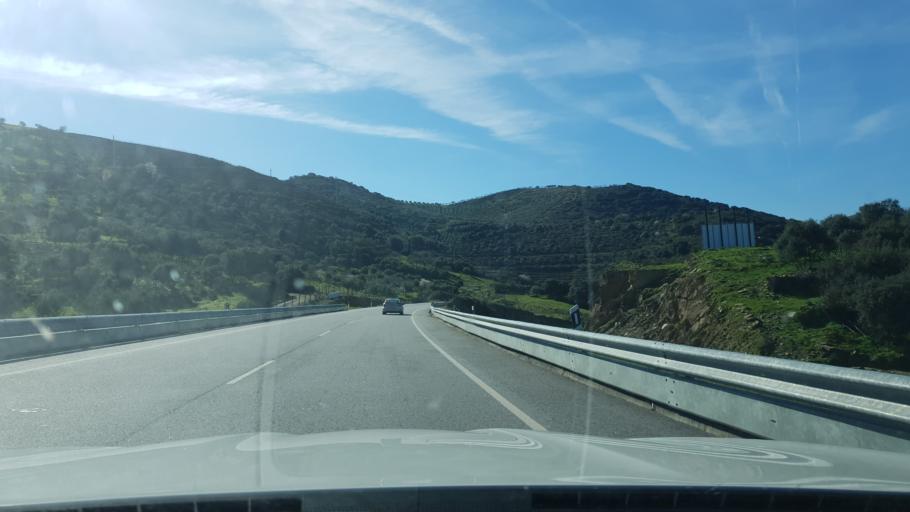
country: PT
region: Braganca
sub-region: Torre de Moncorvo
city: Torre de Moncorvo
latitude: 41.2059
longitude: -7.0813
